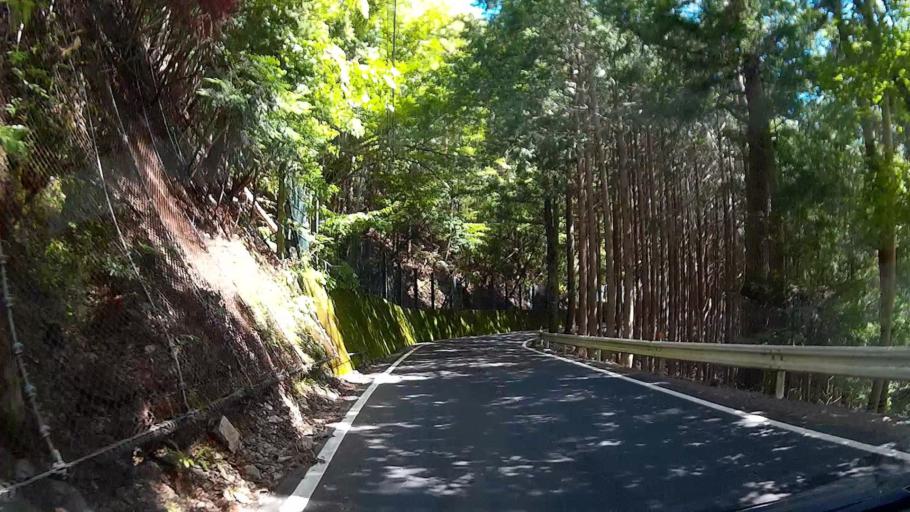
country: JP
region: Shizuoka
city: Shizuoka-shi
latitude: 35.2067
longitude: 138.2328
